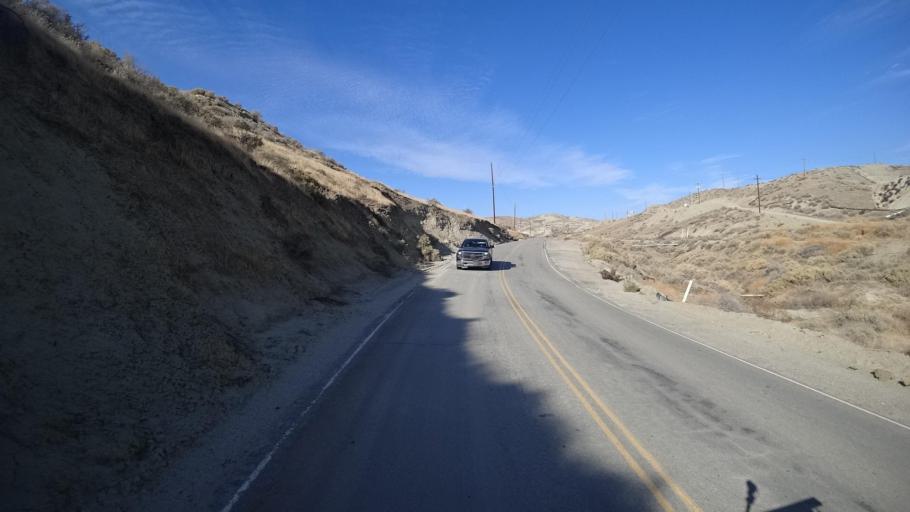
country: US
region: California
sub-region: Kern County
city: Oildale
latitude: 35.5729
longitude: -118.9596
